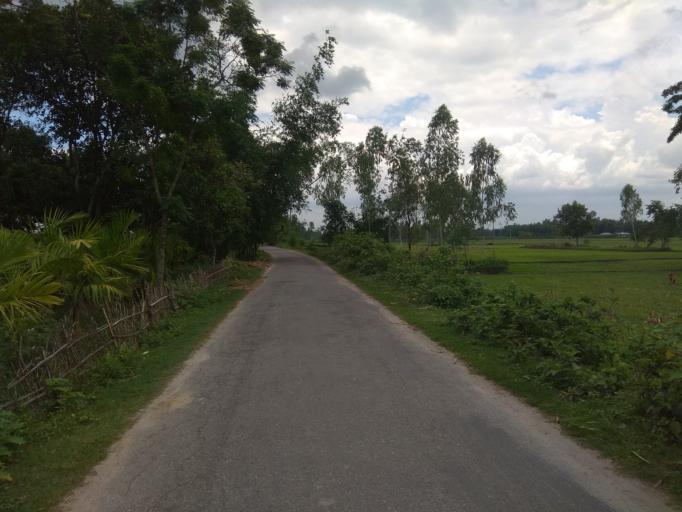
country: IN
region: West Bengal
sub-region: Koch Bihar
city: Haldibari
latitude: 26.2023
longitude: 88.9213
